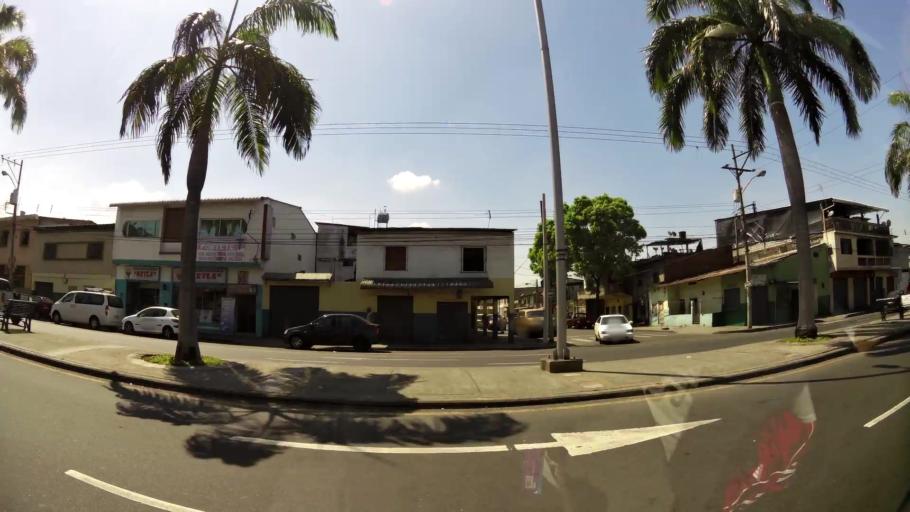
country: EC
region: Guayas
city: Guayaquil
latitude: -2.1988
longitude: -79.9282
